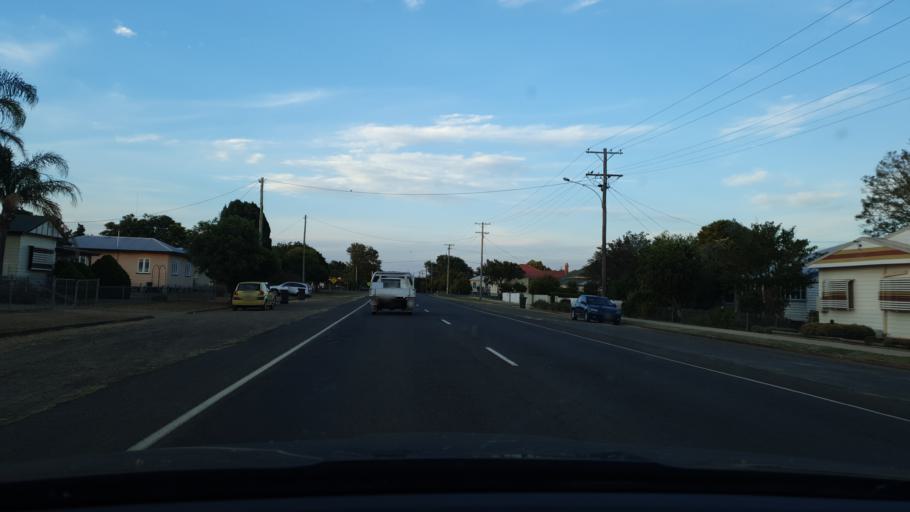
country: AU
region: Queensland
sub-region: Southern Downs
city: Warwick
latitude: -28.0345
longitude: 151.9805
